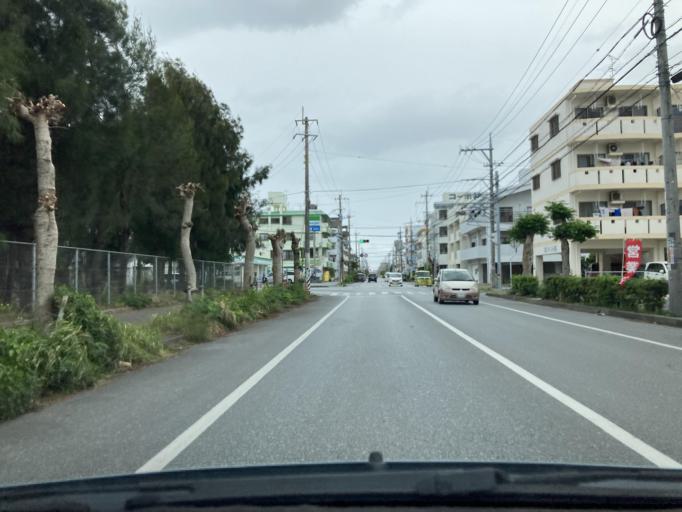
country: JP
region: Okinawa
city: Itoman
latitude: 26.1384
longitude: 127.6668
